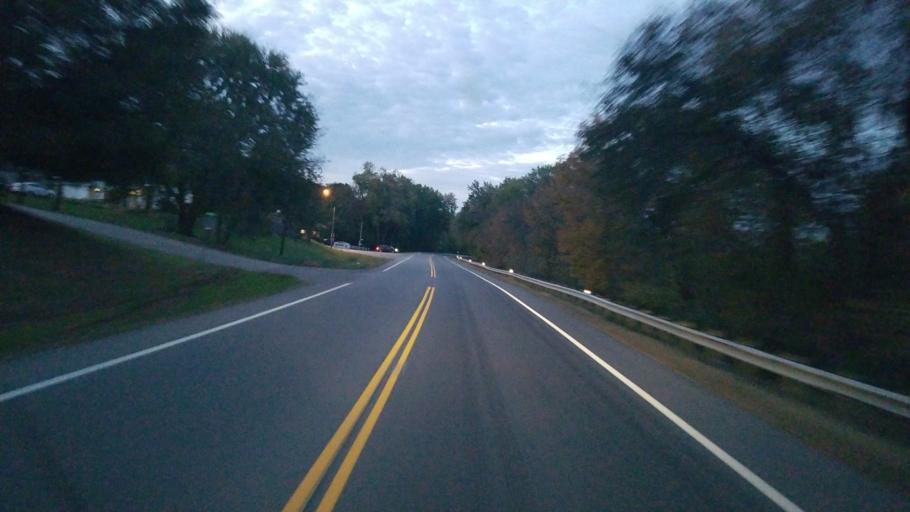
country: US
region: Ohio
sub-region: Scioto County
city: West Portsmouth
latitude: 38.7873
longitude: -83.0132
